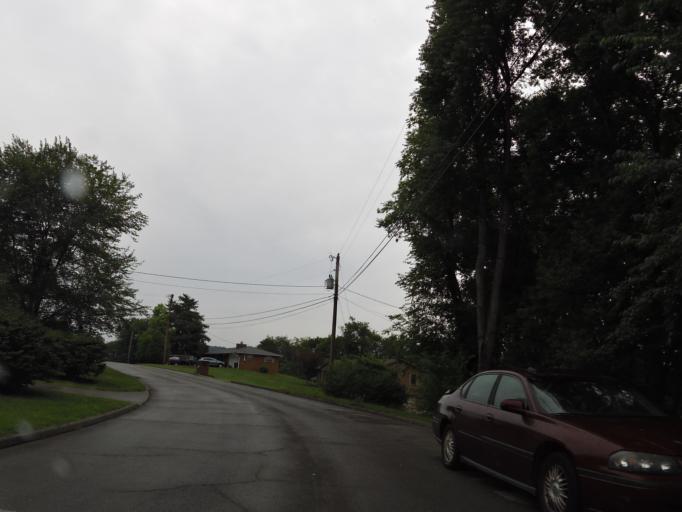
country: US
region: Tennessee
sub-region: Blount County
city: Eagleton Village
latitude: 35.8374
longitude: -83.9531
